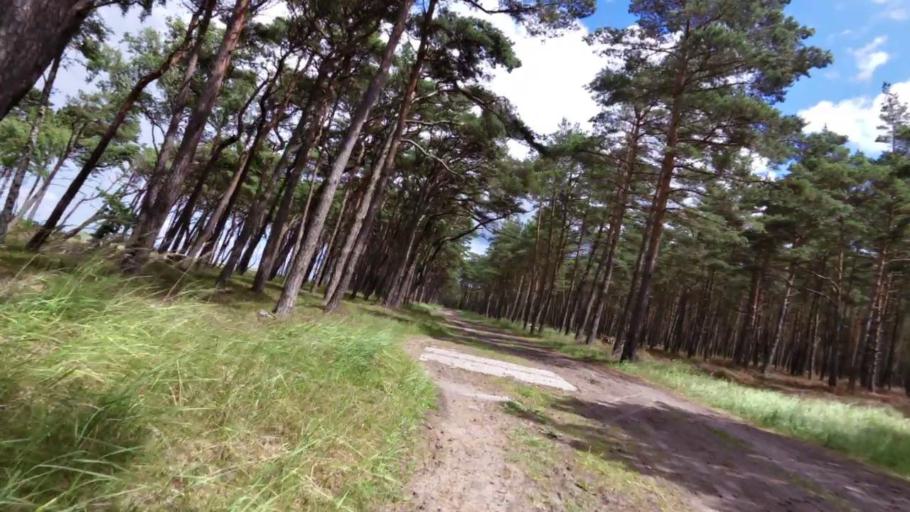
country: PL
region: West Pomeranian Voivodeship
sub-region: Powiat slawienski
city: Darlowo
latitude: 54.4967
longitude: 16.4488
